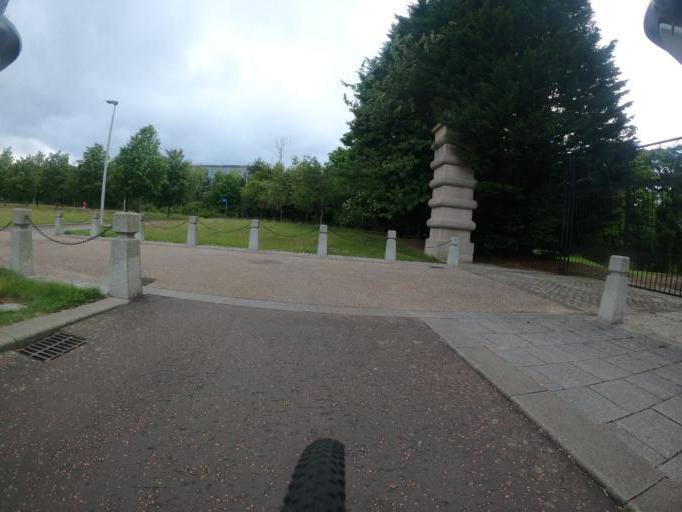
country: GB
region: Scotland
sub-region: Edinburgh
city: Edinburgh
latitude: 55.9805
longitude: -3.2401
